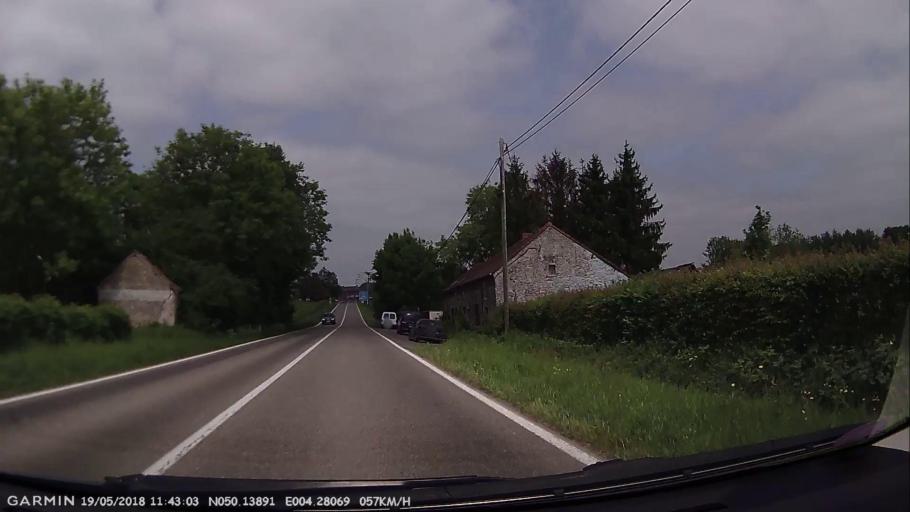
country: BE
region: Wallonia
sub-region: Province du Hainaut
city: Froidchapelle
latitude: 50.1391
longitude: 4.2805
